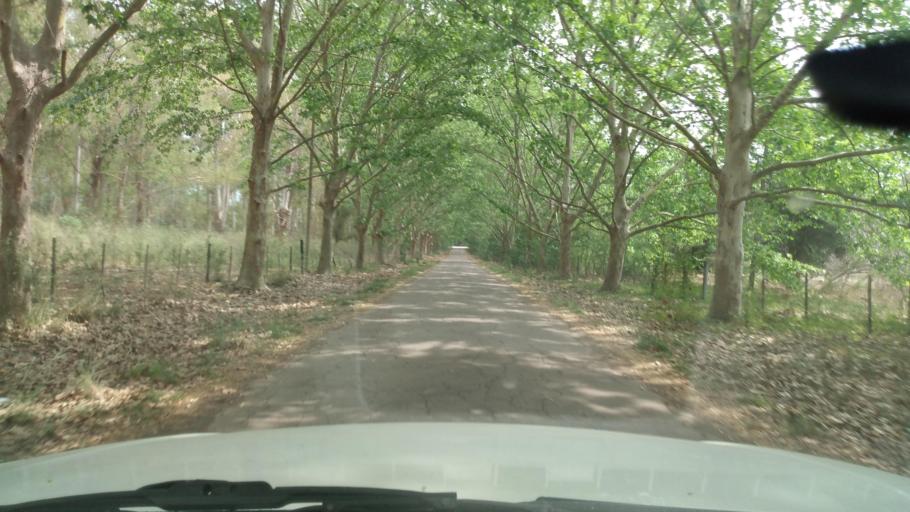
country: AR
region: Buenos Aires
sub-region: Partido de Lujan
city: Lujan
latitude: -34.5559
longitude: -59.1891
